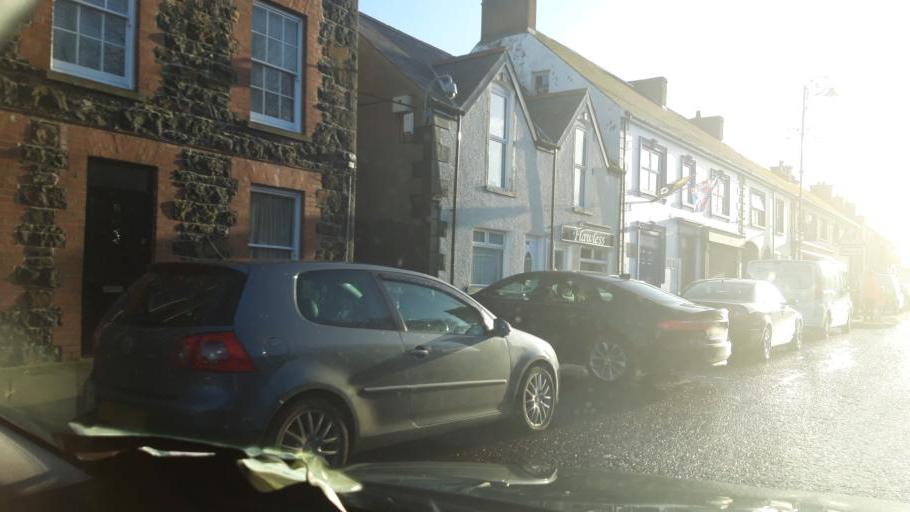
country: GB
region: Northern Ireland
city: Garvagh
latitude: 54.9824
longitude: -6.6877
